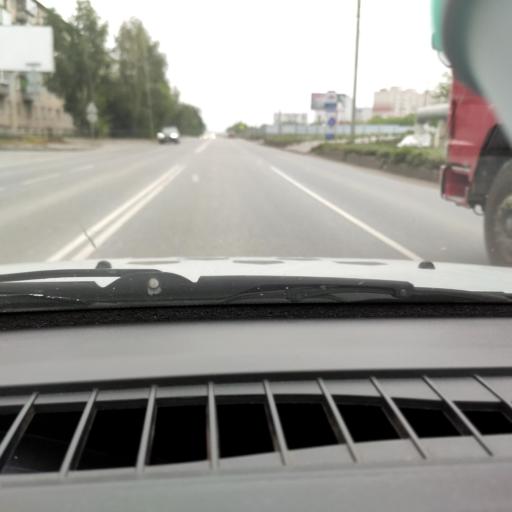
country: RU
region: Chelyabinsk
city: Miass
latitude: 55.0508
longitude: 60.1038
